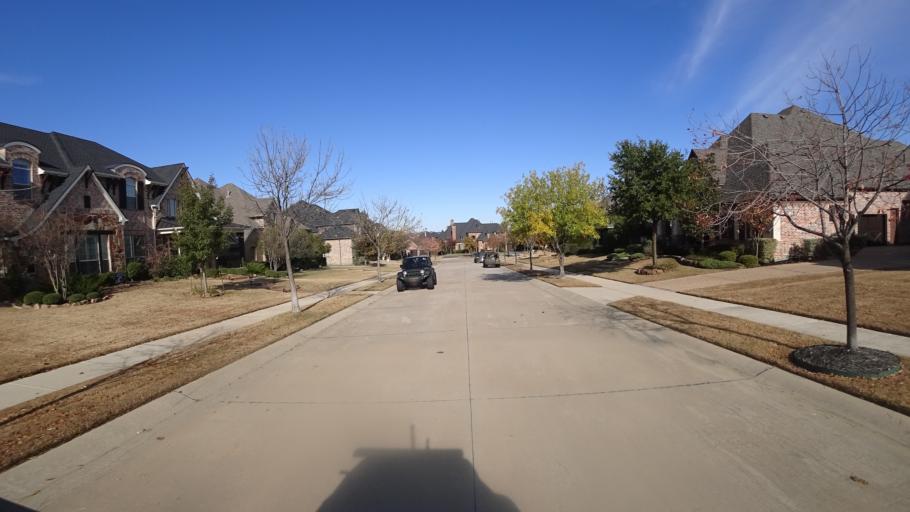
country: US
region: Texas
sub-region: Denton County
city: The Colony
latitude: 33.0282
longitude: -96.9070
